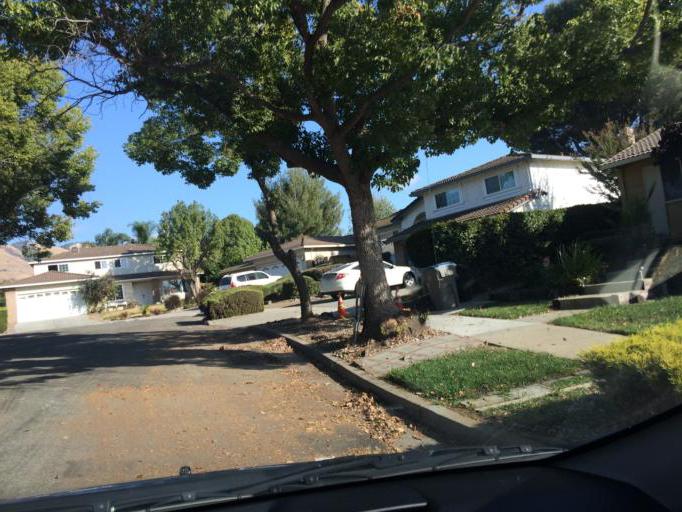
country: US
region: California
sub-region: Santa Clara County
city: Alum Rock
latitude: 37.3335
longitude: -121.7886
